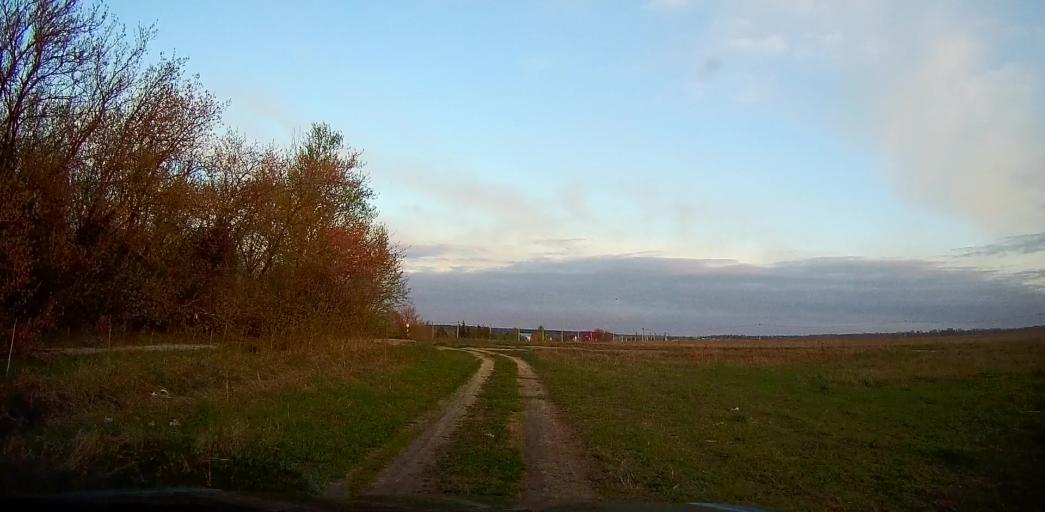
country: RU
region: Moskovskaya
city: Peski
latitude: 55.2320
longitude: 38.7311
